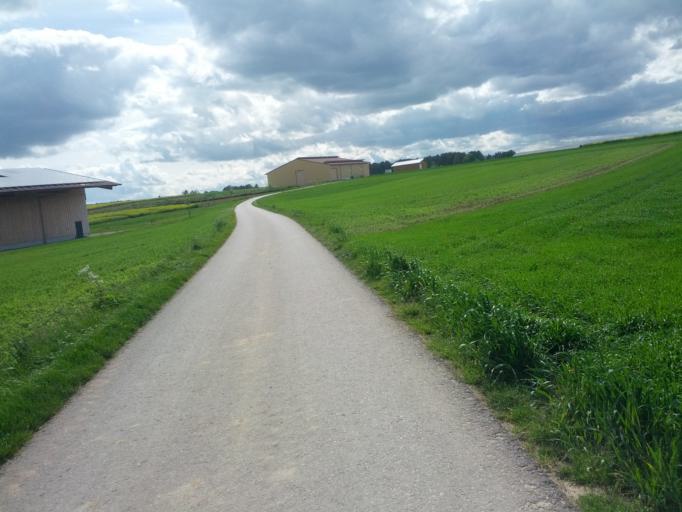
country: DE
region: Baden-Wuerttemberg
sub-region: Regierungsbezirk Stuttgart
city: Magstadt
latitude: 48.7106
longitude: 8.9341
